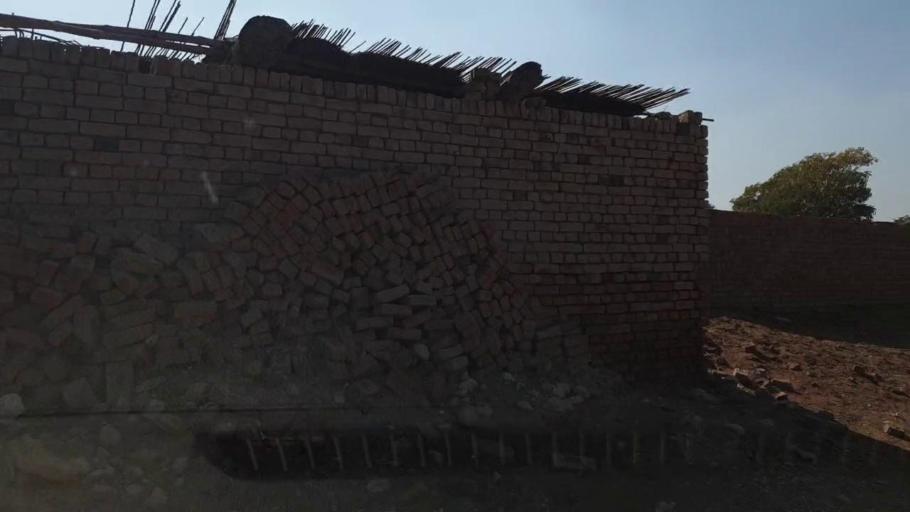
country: PK
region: Sindh
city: Bhit Shah
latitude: 25.9243
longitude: 68.4845
